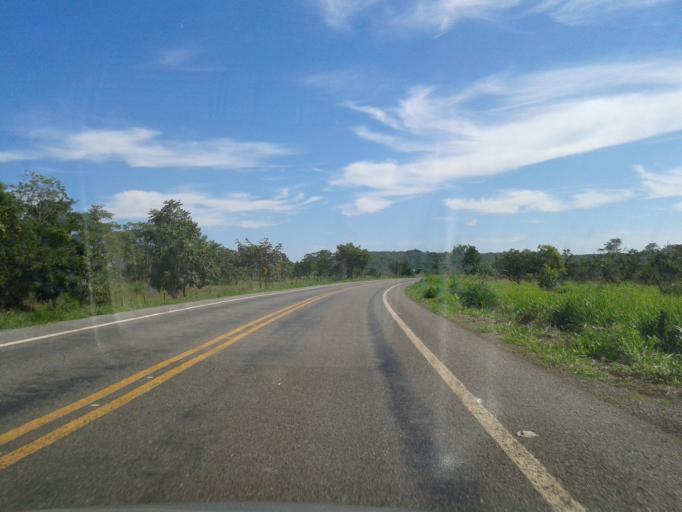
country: BR
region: Goias
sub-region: Piracanjuba
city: Piracanjuba
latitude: -17.2943
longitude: -48.7899
